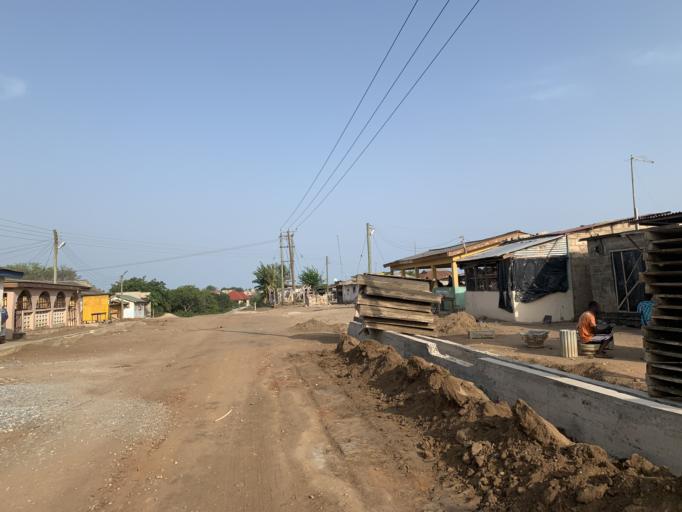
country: GH
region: Central
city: Winneba
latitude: 5.3784
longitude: -0.6144
